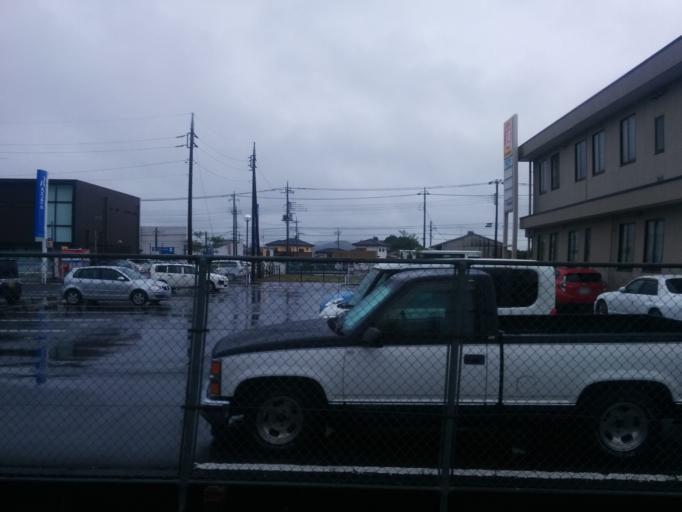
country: JP
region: Tochigi
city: Kanuma
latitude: 36.5716
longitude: 139.7627
